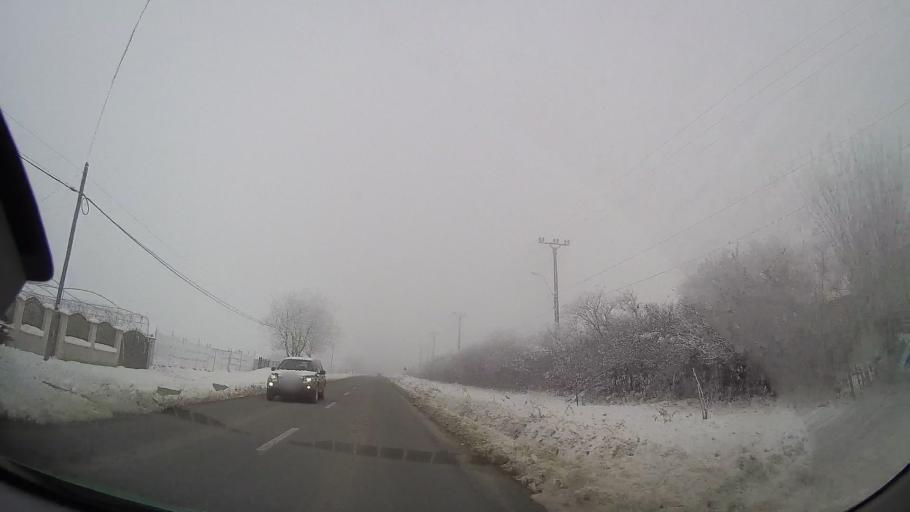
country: RO
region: Iasi
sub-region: Comuna Stolniceni-Prajescu
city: Stolniceni-Prajescu
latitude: 47.1973
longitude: 26.7389
